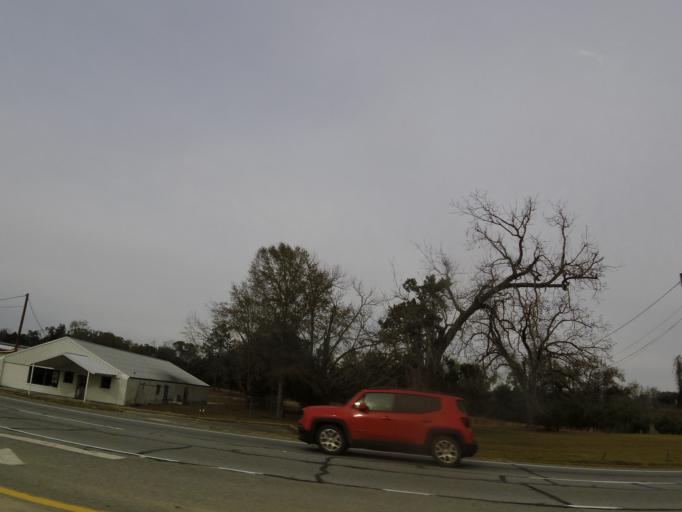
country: US
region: Georgia
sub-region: Decatur County
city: Bainbridge
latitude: 30.9209
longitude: -84.6047
